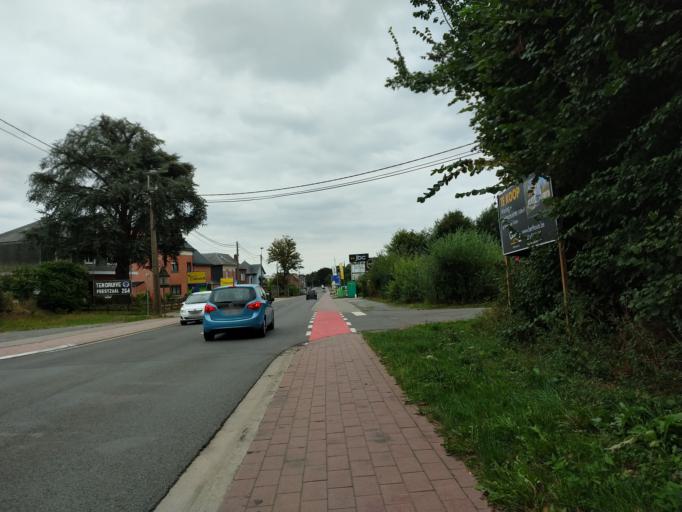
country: BE
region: Flanders
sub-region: Provincie Vlaams-Brabant
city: Overijse
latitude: 50.7800
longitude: 4.5168
